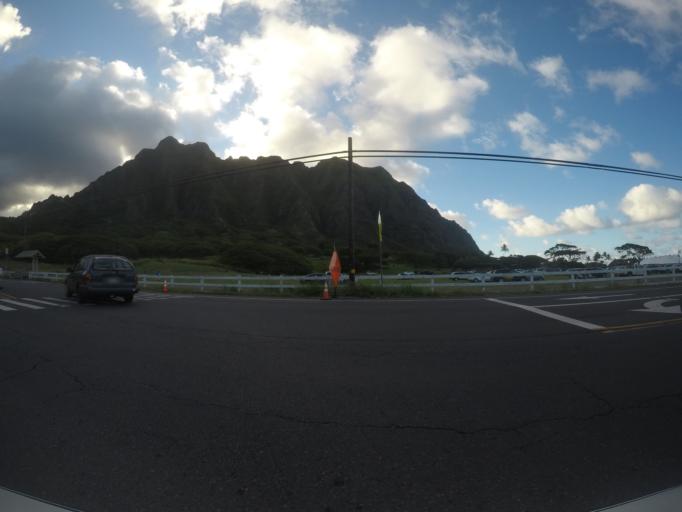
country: US
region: Hawaii
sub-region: Honolulu County
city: Ka'a'awa
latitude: 21.5170
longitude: -157.8377
